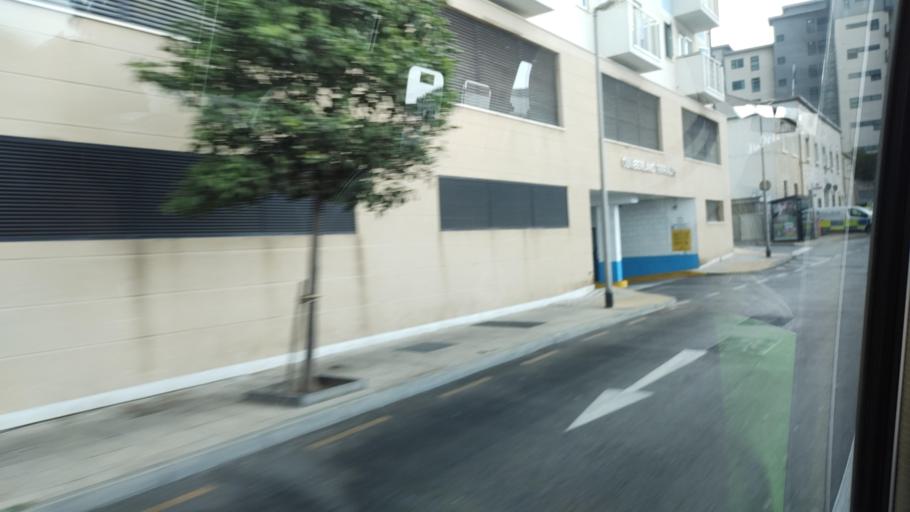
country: GI
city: Gibraltar
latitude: 36.1246
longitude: -5.3536
